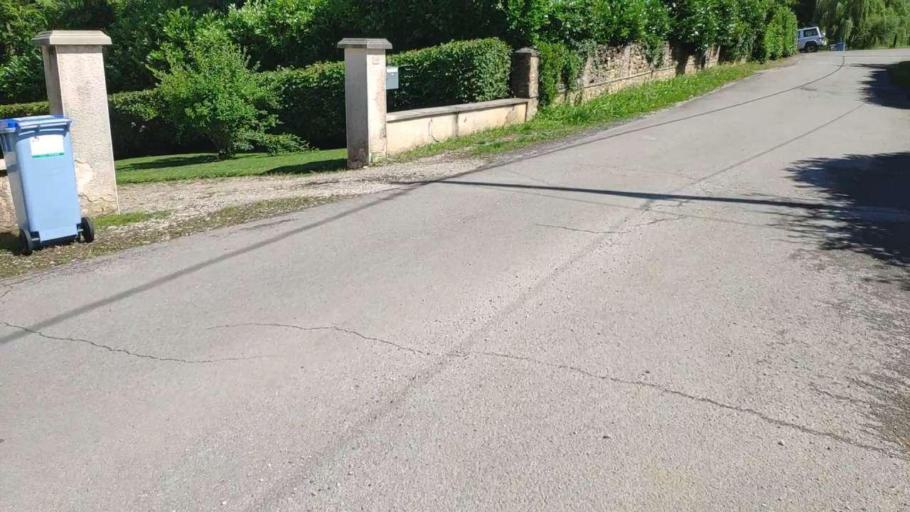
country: FR
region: Franche-Comte
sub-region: Departement du Jura
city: Bletterans
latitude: 46.7998
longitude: 5.5610
